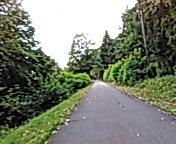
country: LU
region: Grevenmacher
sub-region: Canton d'Echternach
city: Mompach
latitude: 49.7531
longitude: 6.5002
